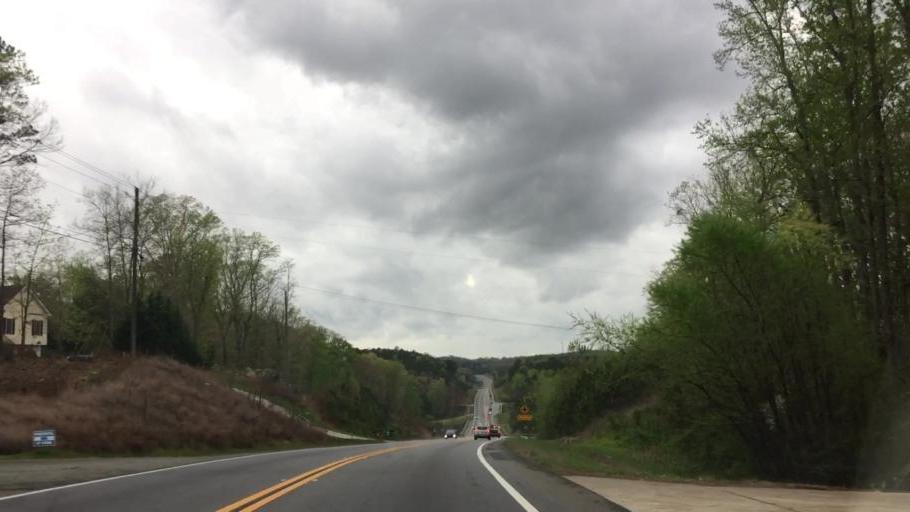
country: US
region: Georgia
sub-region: Bartow County
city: Emerson
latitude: 34.2208
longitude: -84.7172
